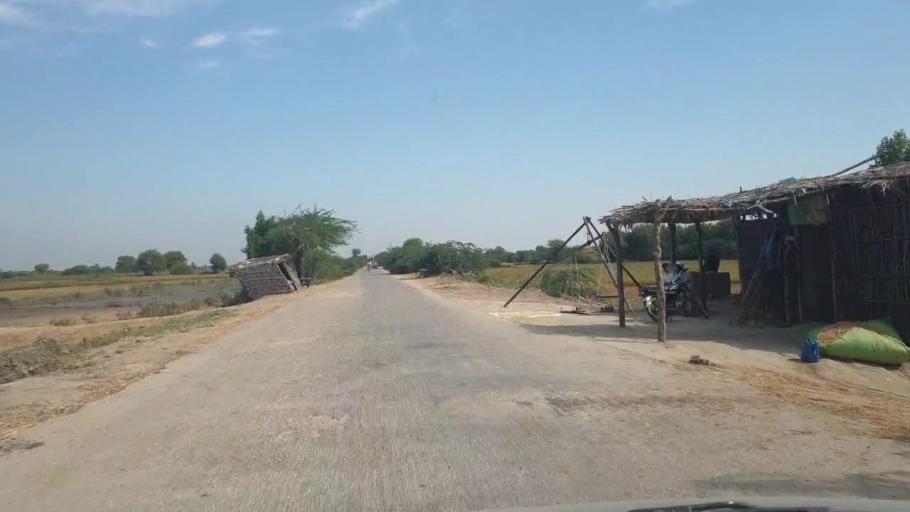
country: PK
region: Sindh
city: Tando Bago
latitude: 24.9000
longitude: 69.0154
